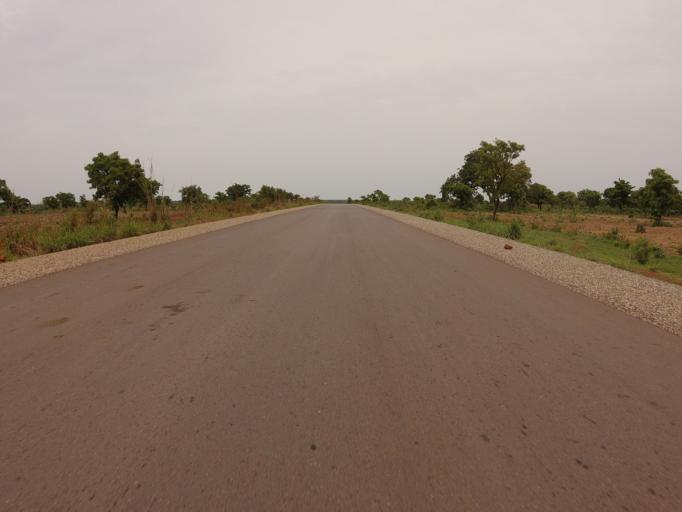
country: GH
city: Kpandae
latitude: 8.9504
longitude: -0.0178
